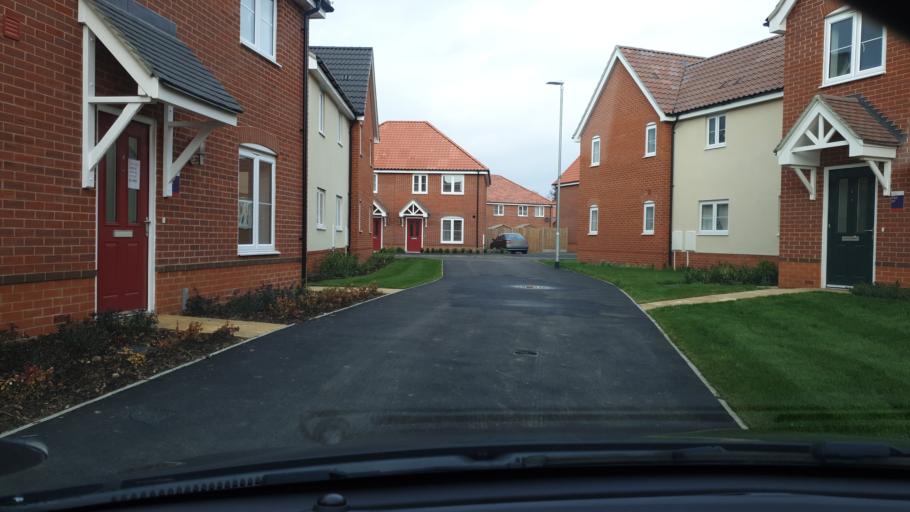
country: GB
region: England
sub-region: Essex
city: Alresford
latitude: 51.8549
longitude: 0.9950
